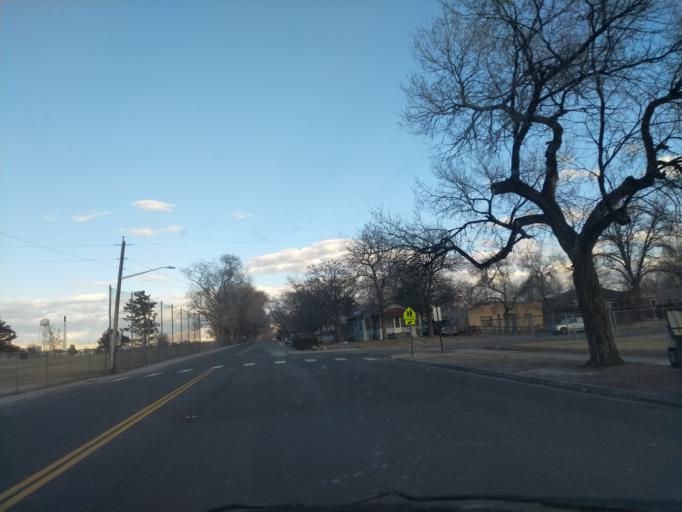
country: US
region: Colorado
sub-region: Mesa County
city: Grand Junction
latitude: 39.0734
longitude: -108.5483
